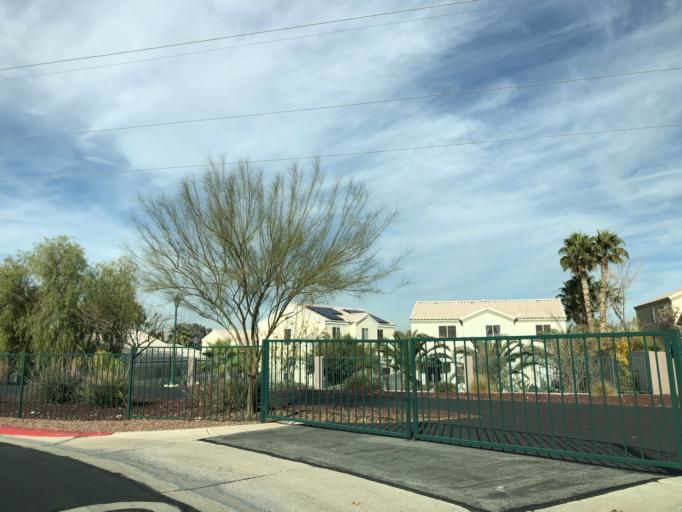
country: US
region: Nevada
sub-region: Clark County
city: Whitney
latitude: 36.0149
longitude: -115.0945
